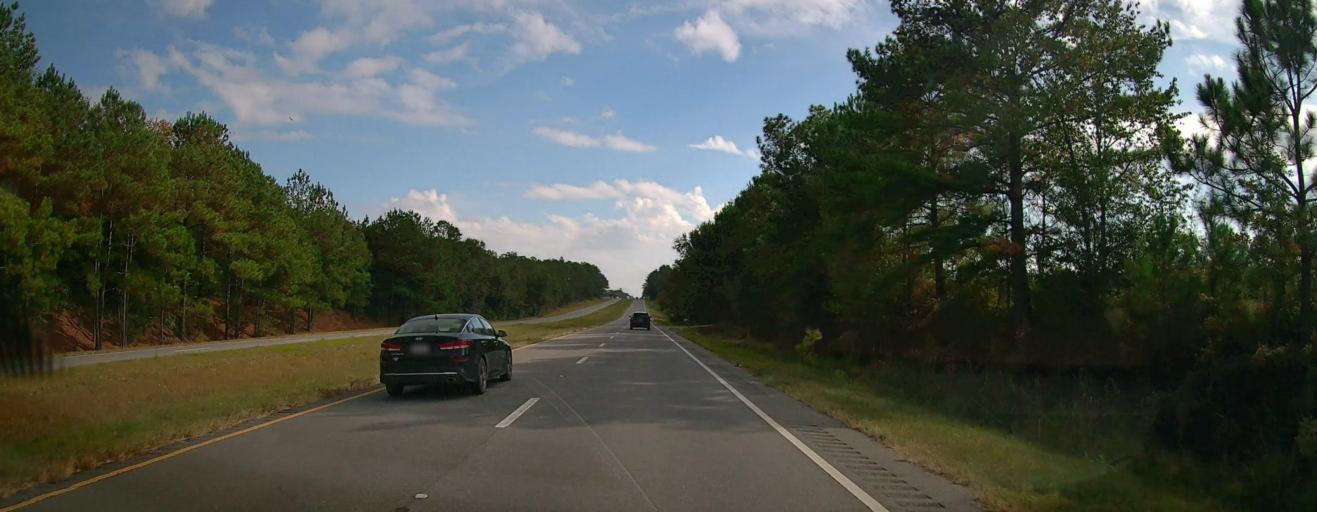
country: US
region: Georgia
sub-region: Thomas County
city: Meigs
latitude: 30.9850
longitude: -84.0409
